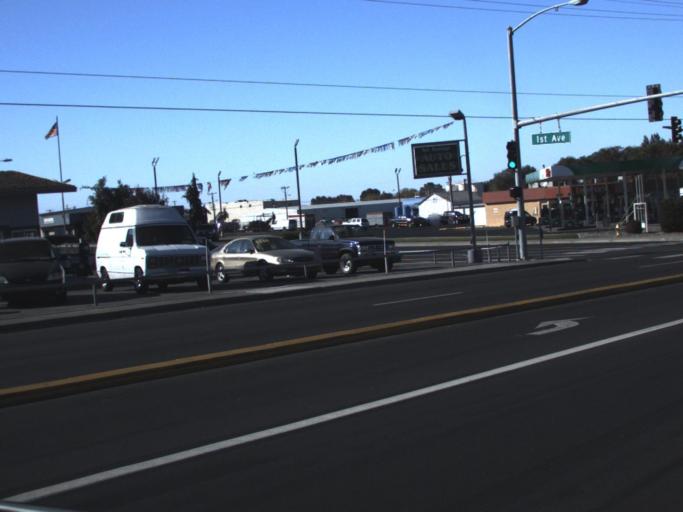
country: US
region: Washington
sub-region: Benton County
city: Kennewick
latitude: 46.2072
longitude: -119.1070
